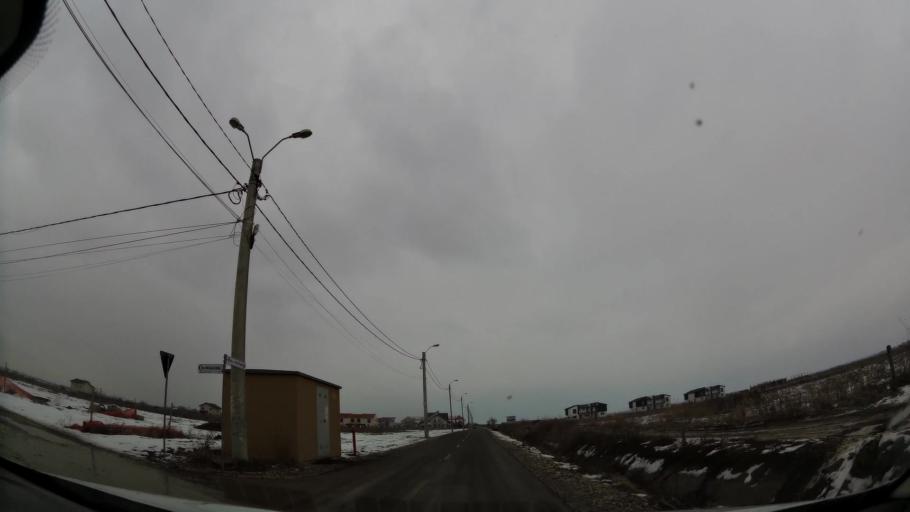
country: RO
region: Ilfov
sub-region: Comuna Otopeni
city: Otopeni
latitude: 44.5539
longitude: 26.1069
